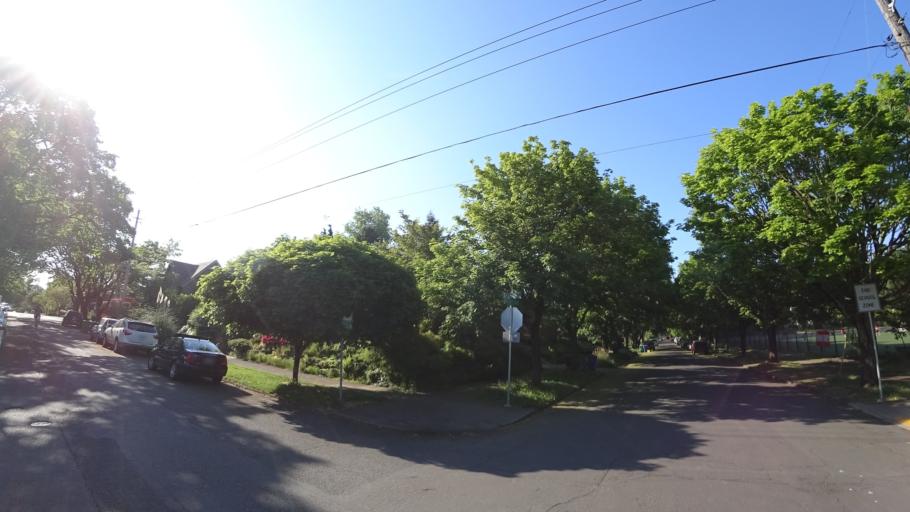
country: US
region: Oregon
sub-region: Multnomah County
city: Portland
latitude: 45.5467
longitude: -122.6421
